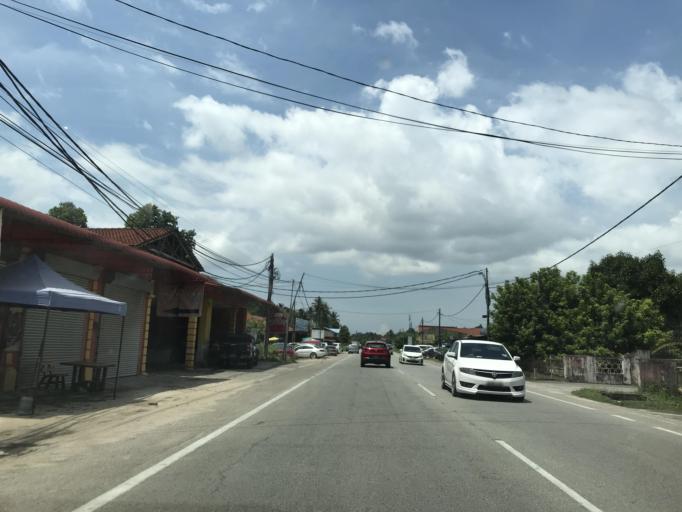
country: MY
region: Kelantan
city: Pasir Mas
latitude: 6.0578
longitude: 102.1992
